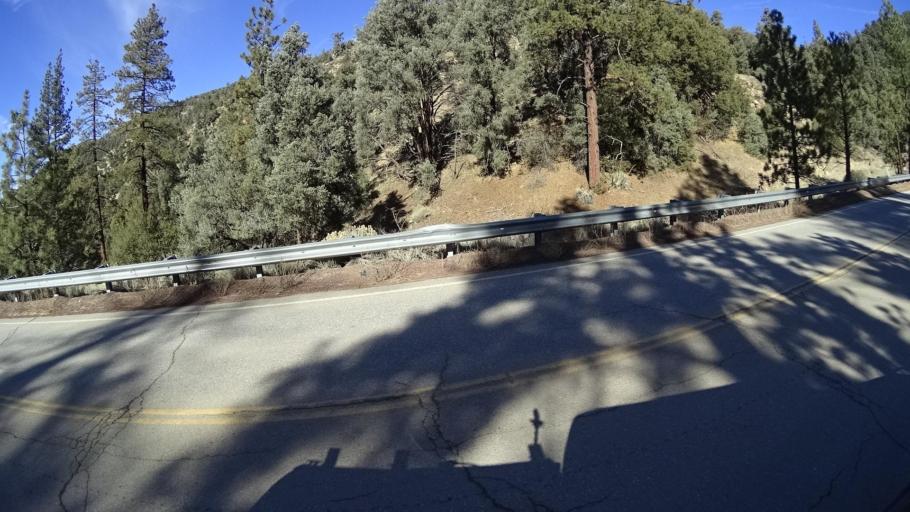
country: US
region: California
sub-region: Kern County
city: Pine Mountain Club
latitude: 34.8480
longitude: -119.0922
